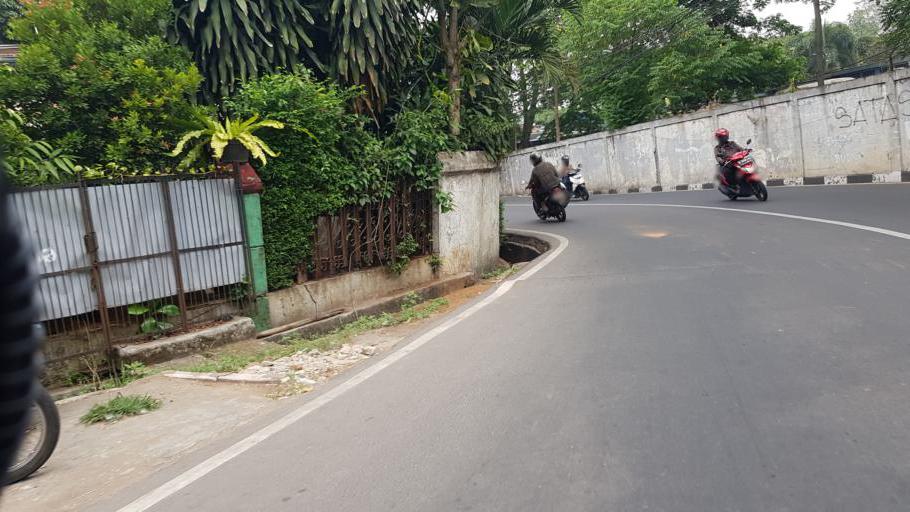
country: ID
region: West Java
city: Pamulang
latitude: -6.3054
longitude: 106.8190
